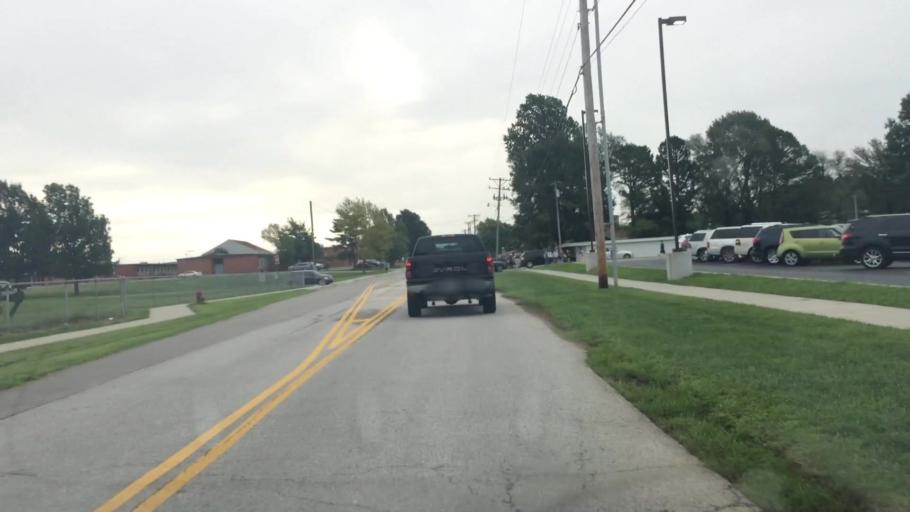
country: US
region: Missouri
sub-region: Greene County
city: Strafford
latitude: 37.2707
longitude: -93.1228
